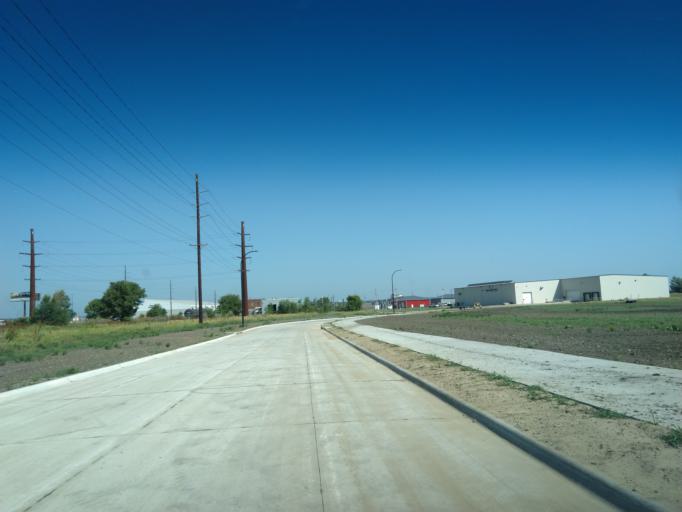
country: US
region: Iowa
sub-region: Woodbury County
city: Sioux City
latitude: 42.4793
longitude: -96.3850
